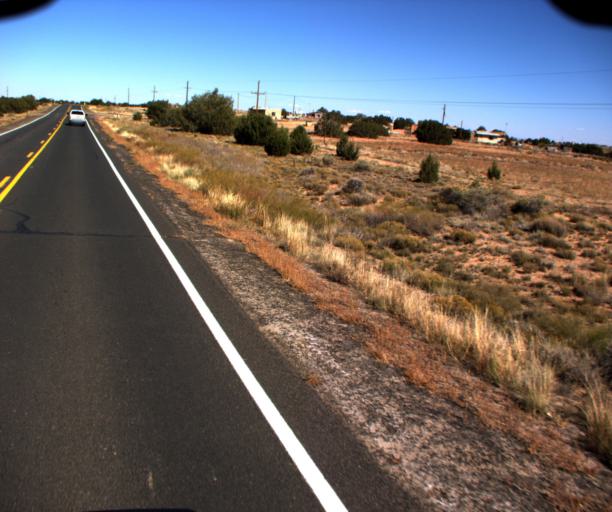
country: US
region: Arizona
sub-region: Navajo County
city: First Mesa
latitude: 35.8314
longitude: -110.5305
